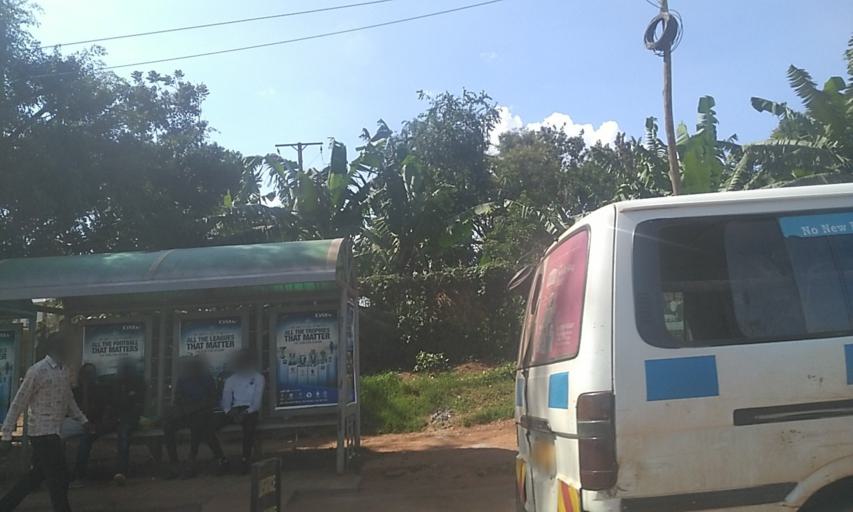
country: UG
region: Central Region
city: Kampala Central Division
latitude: 0.3353
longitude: 32.5777
